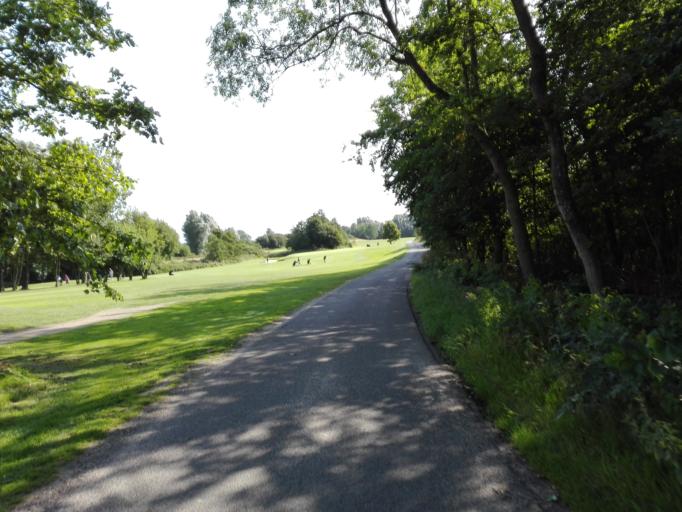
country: DK
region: Central Jutland
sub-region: Arhus Kommune
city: Lystrup
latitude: 56.2131
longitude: 10.1954
